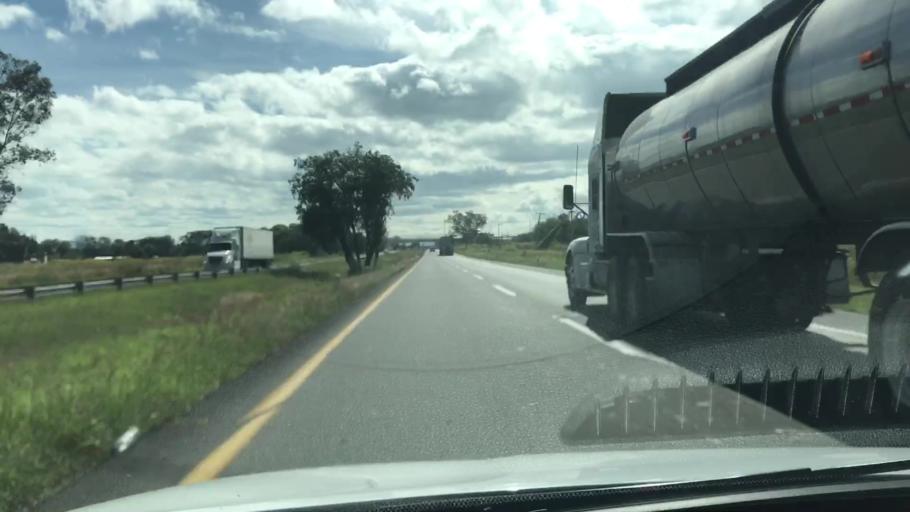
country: MX
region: Guanajuato
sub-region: Leon
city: San Jose de Duran (Los Troncoso)
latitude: 21.0735
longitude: -101.6985
